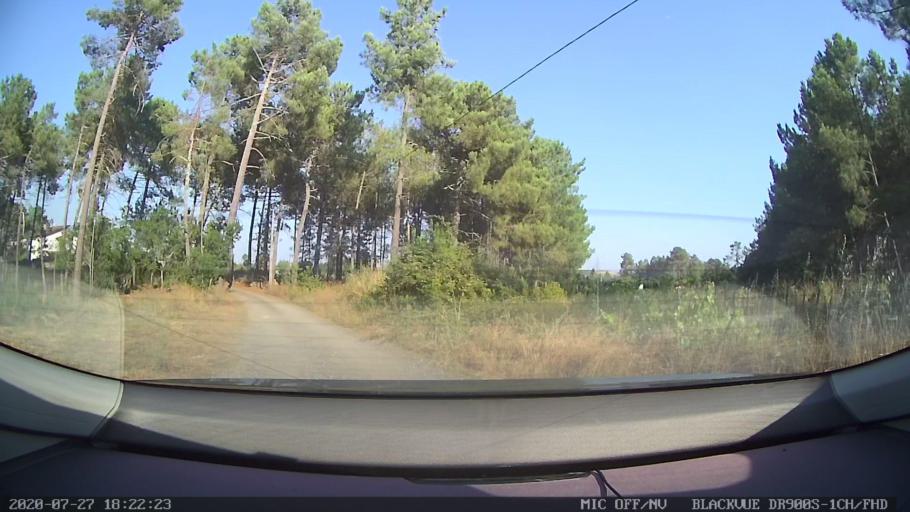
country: PT
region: Vila Real
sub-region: Vila Real
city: Vila Real
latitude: 41.2724
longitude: -7.7292
